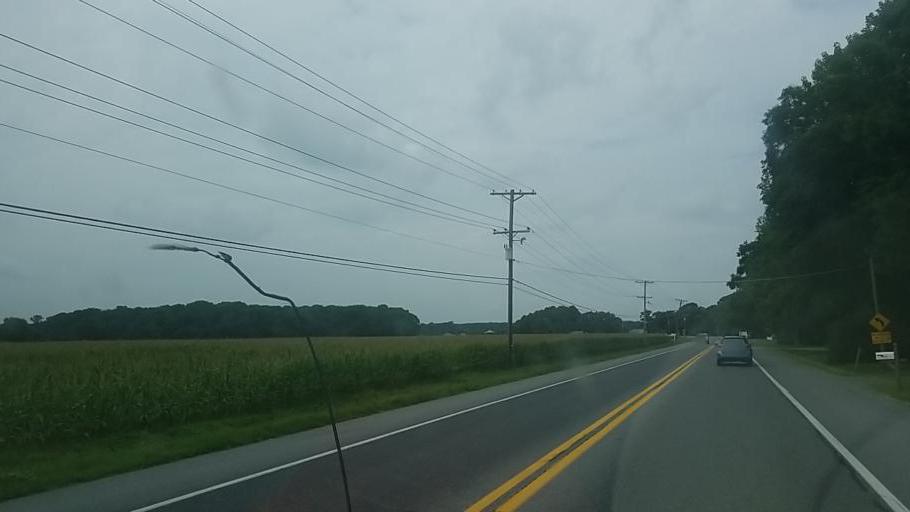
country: US
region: Delaware
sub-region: Sussex County
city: Long Neck
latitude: 38.5564
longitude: -75.1614
